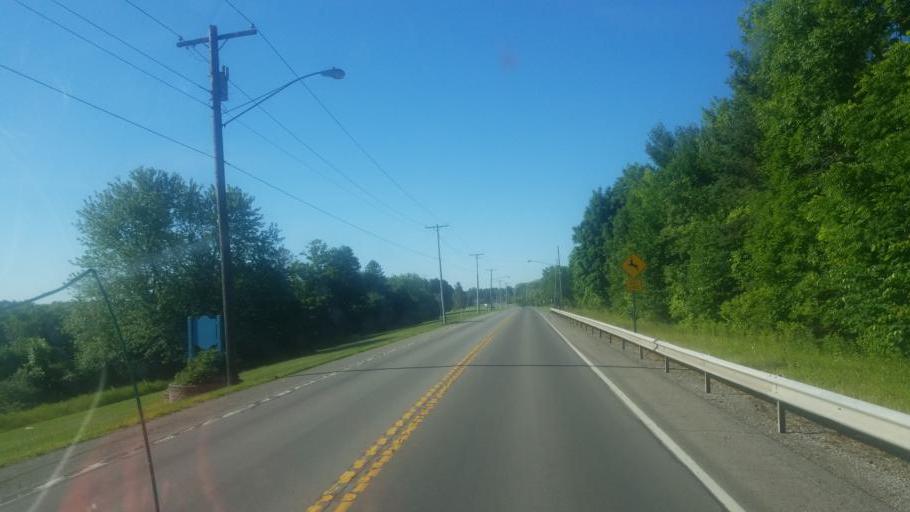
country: US
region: New York
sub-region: Wayne County
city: Newark
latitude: 43.0289
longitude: -77.0964
